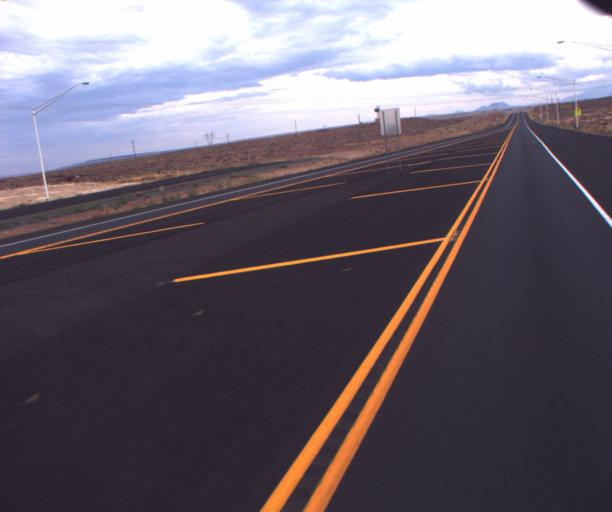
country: US
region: Arizona
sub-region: Coconino County
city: Tuba City
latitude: 35.8362
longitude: -111.4368
